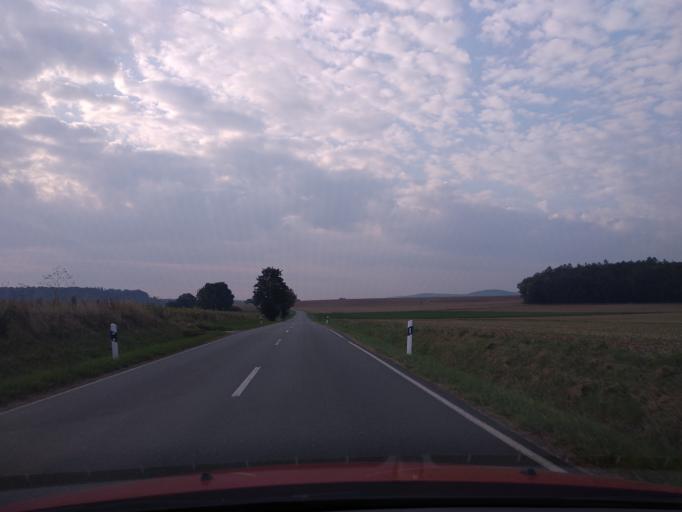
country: DE
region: Hesse
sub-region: Regierungsbezirk Kassel
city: Calden
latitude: 51.4227
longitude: 9.3389
